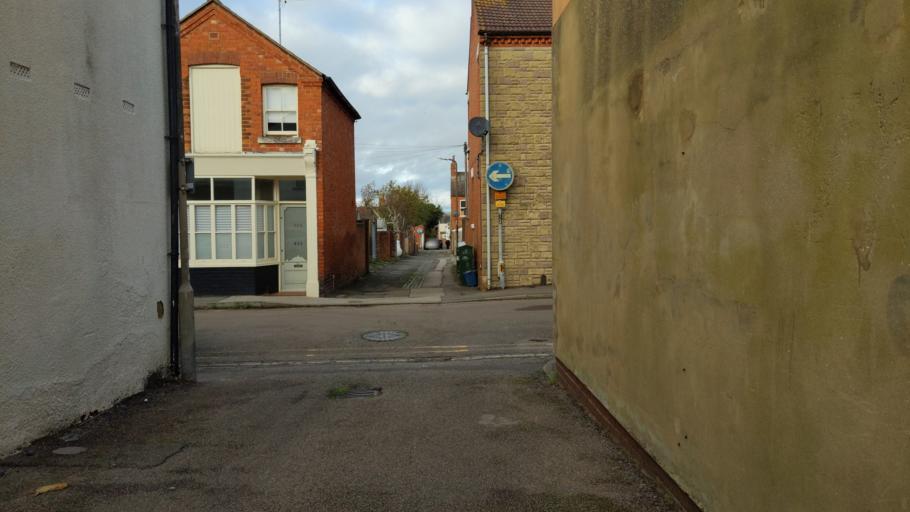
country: GB
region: England
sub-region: Milton Keynes
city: Bradwell
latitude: 52.0606
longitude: -0.8124
